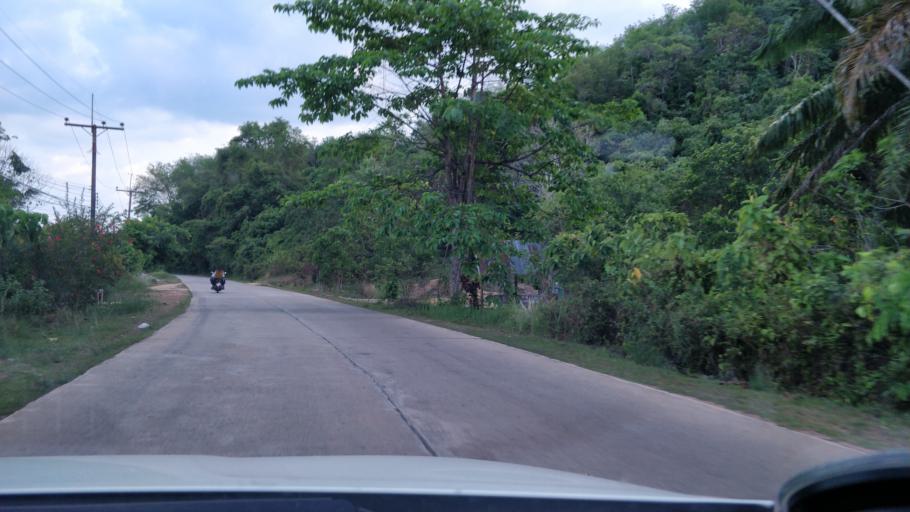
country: TH
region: Krabi
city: Saladan
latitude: 7.5799
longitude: 99.0675
